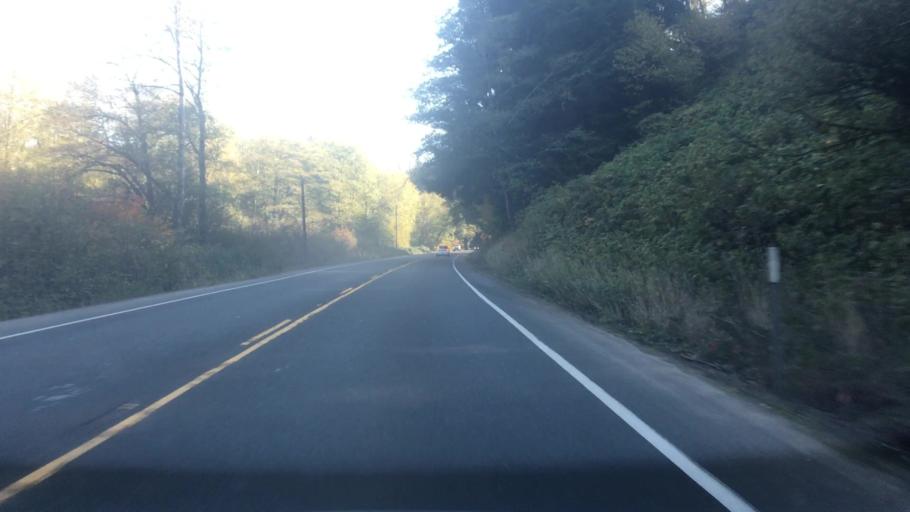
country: US
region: Oregon
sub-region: Lincoln County
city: Rose Lodge
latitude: 45.0105
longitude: -123.9233
